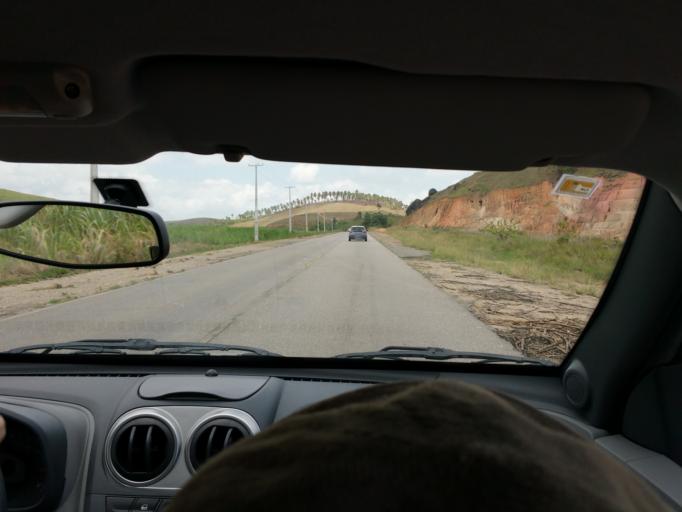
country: BR
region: Pernambuco
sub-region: Sirinhaem
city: Sirinhaem
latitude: -8.6370
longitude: -35.1192
